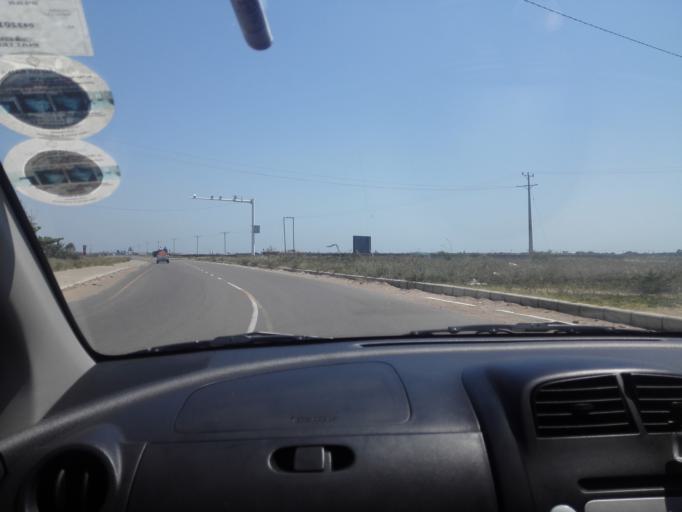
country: MZ
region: Maputo City
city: Maputo
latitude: -25.8475
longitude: 32.6712
